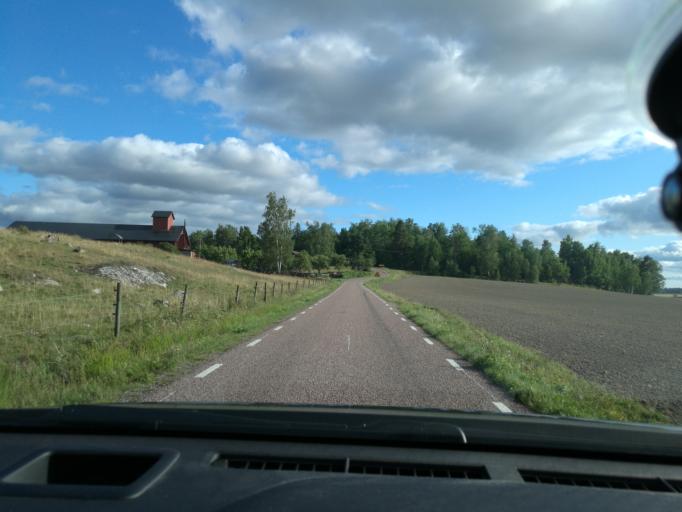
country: SE
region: Vaestmanland
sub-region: Kopings Kommun
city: Koping
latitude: 59.5494
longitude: 16.1081
